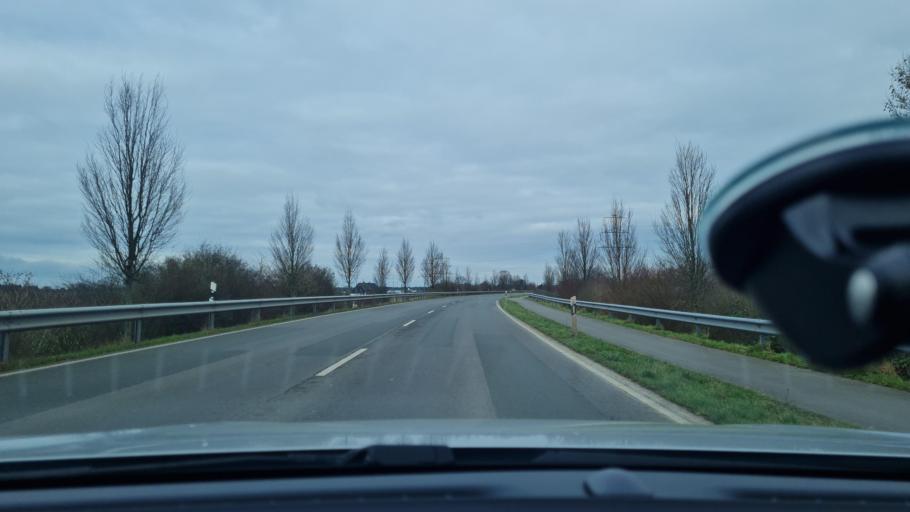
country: DE
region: North Rhine-Westphalia
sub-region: Regierungsbezirk Dusseldorf
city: Voerde
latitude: 51.6048
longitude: 6.6667
